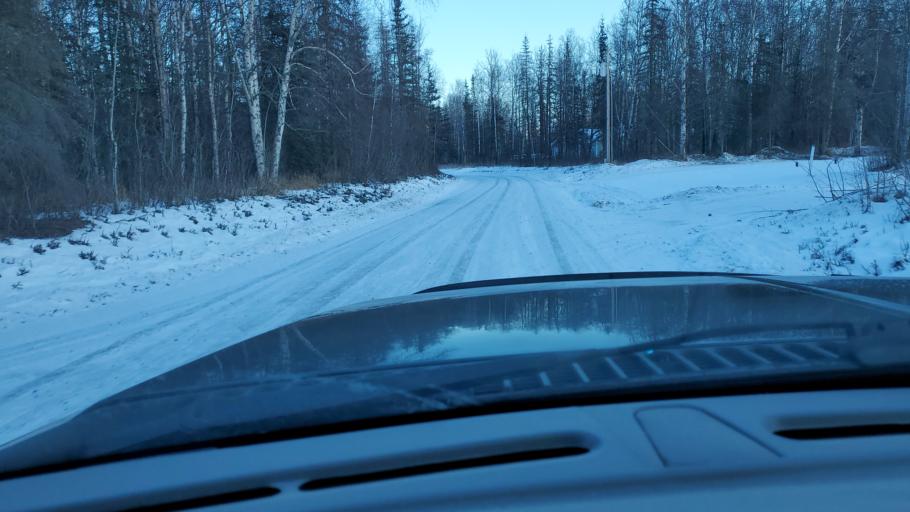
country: US
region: Alaska
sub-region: Matanuska-Susitna Borough
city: Lakes
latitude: 61.6653
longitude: -149.2974
